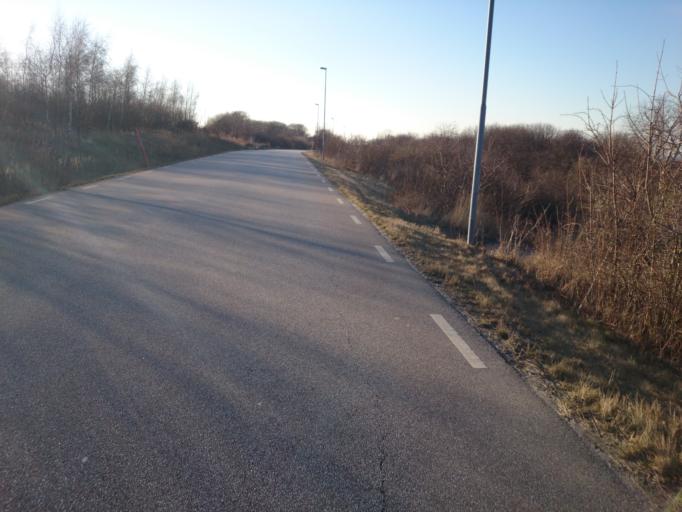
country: SE
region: Skane
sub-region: Malmo
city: Bunkeflostrand
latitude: 55.5689
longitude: 12.9070
